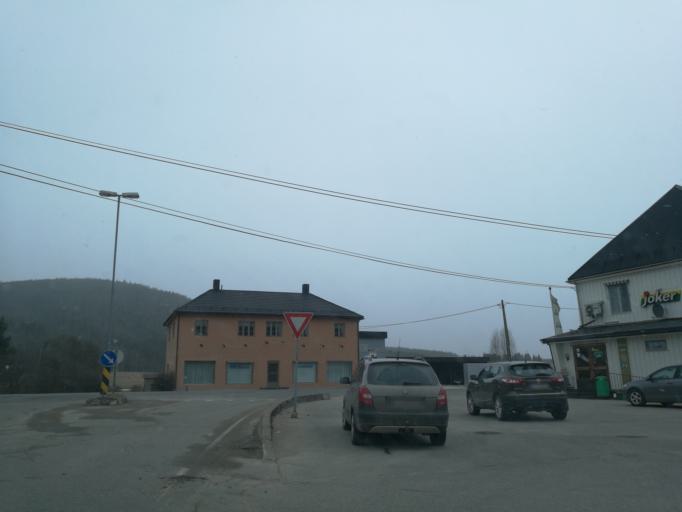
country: NO
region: Hedmark
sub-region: Asnes
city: Flisa
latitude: 60.6408
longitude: 12.0335
